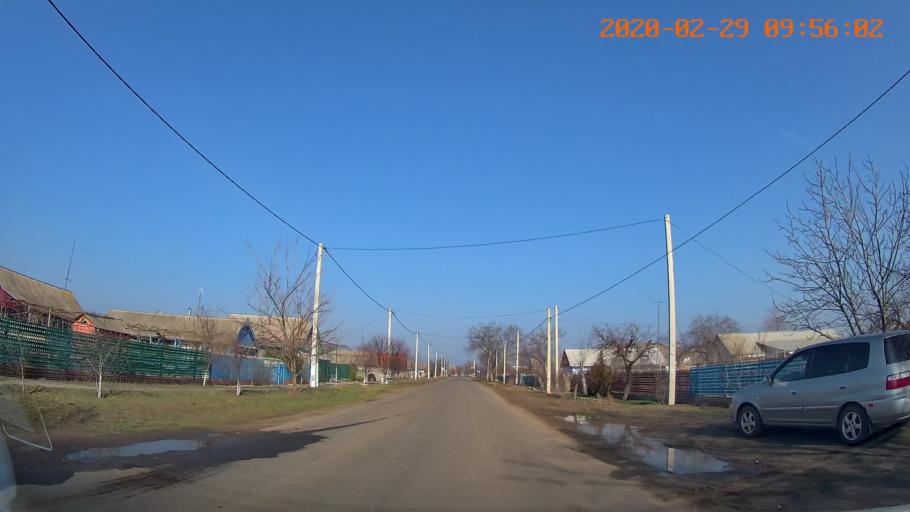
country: MD
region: Telenesti
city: Slobozia
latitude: 46.7390
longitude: 29.7070
